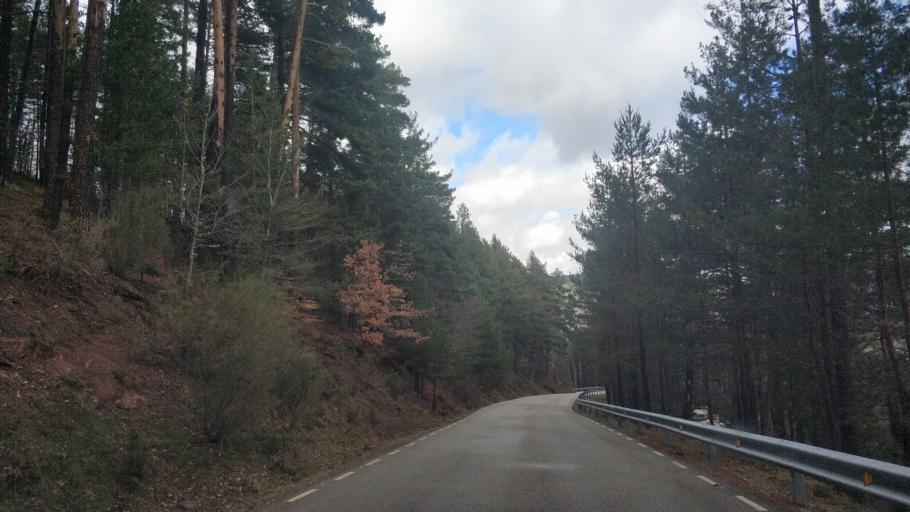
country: ES
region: Castille and Leon
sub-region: Provincia de Burgos
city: Neila
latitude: 42.0448
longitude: -3.0110
